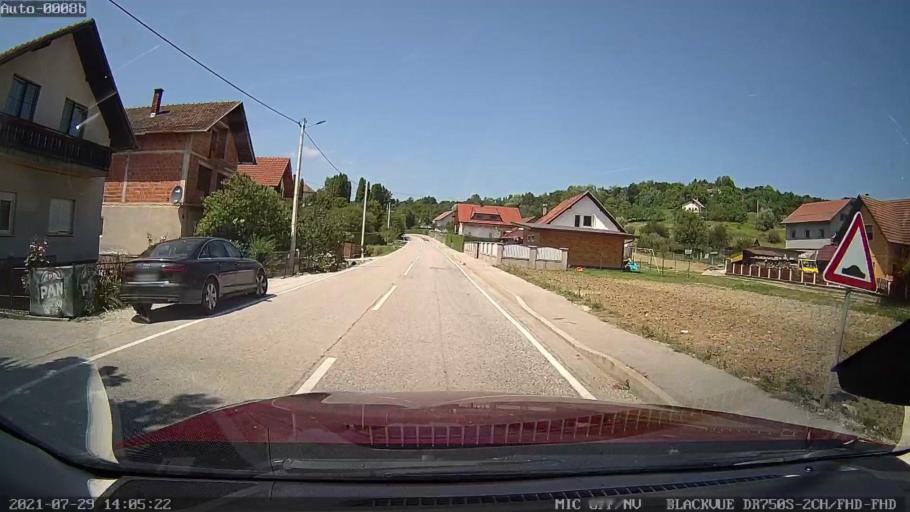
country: HR
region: Varazdinska
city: Lepoglava
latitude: 46.2494
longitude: 15.9589
